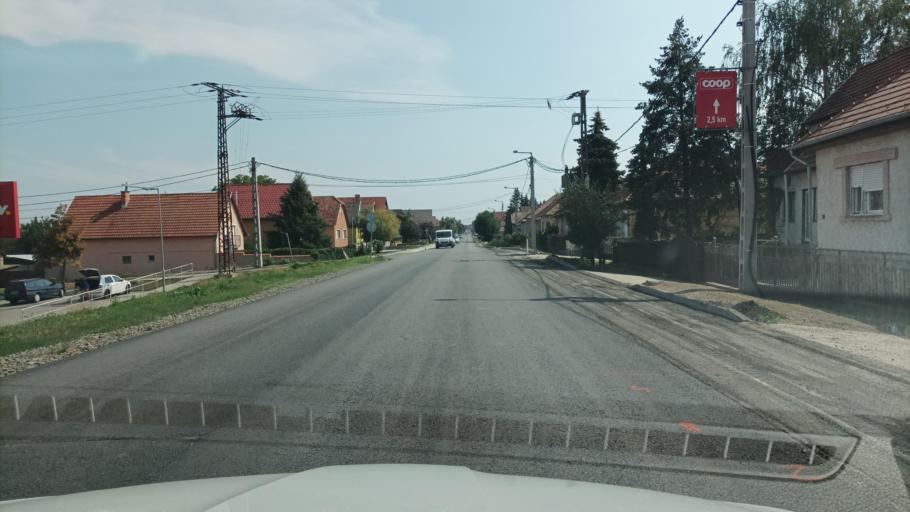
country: HU
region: Pest
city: Galgaheviz
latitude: 47.6166
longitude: 19.5769
